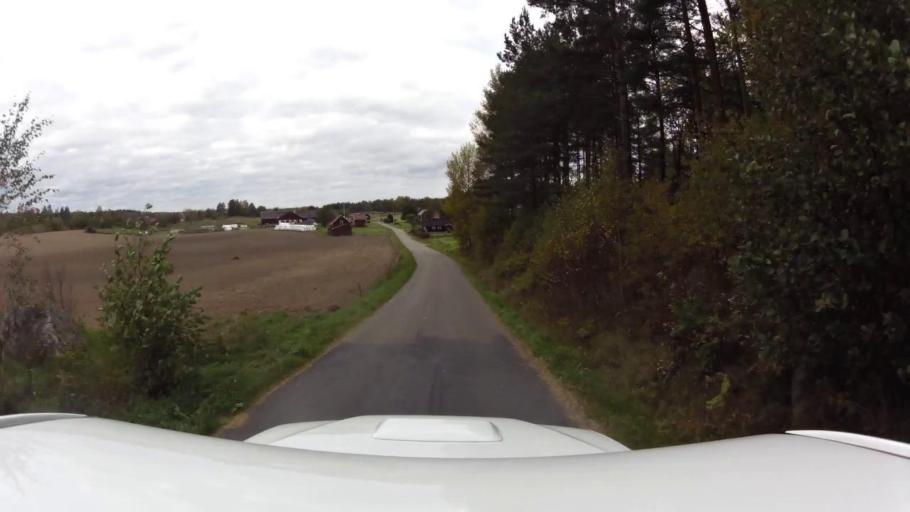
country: SE
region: OEstergoetland
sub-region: Kinda Kommun
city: Rimforsa
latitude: 58.1968
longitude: 15.5800
